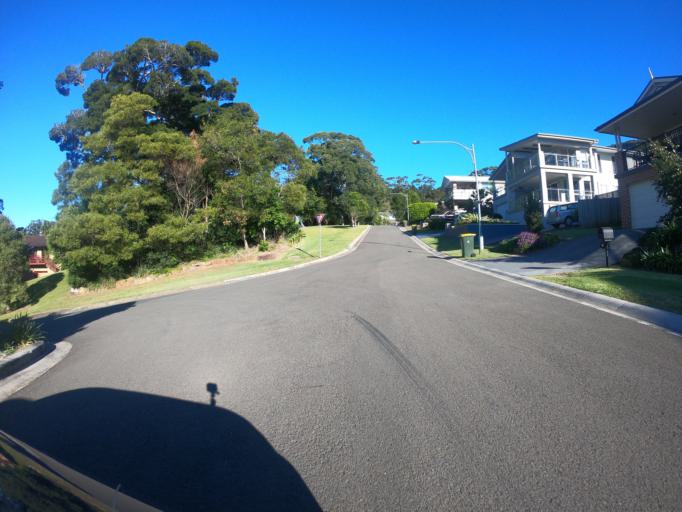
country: AU
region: New South Wales
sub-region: Wollongong
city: Bulli
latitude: -34.3100
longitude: 150.9161
